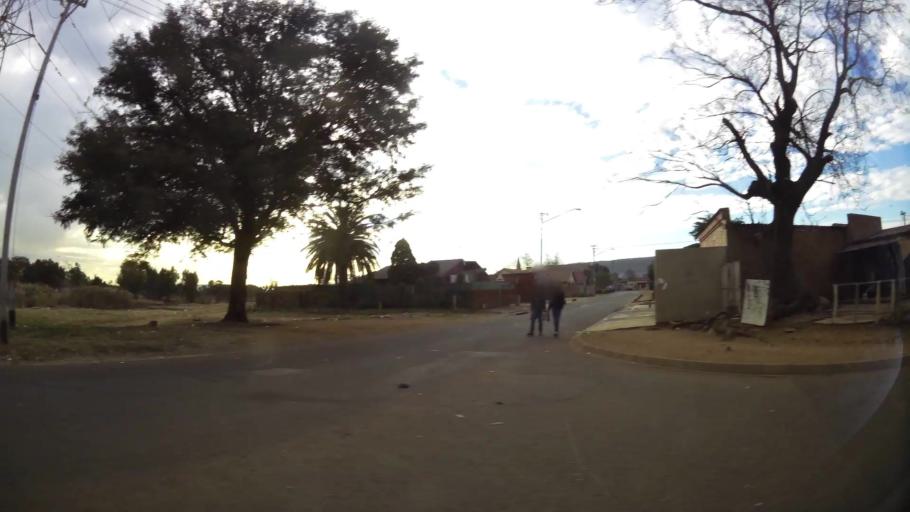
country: ZA
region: Gauteng
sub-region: City of Tshwane Metropolitan Municipality
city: Pretoria
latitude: -25.7136
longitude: 28.3236
